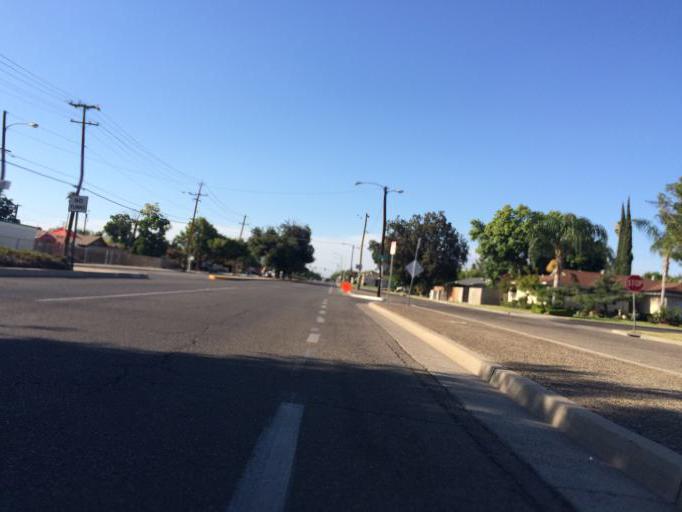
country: US
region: California
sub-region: Fresno County
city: Sunnyside
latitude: 36.7696
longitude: -119.7362
